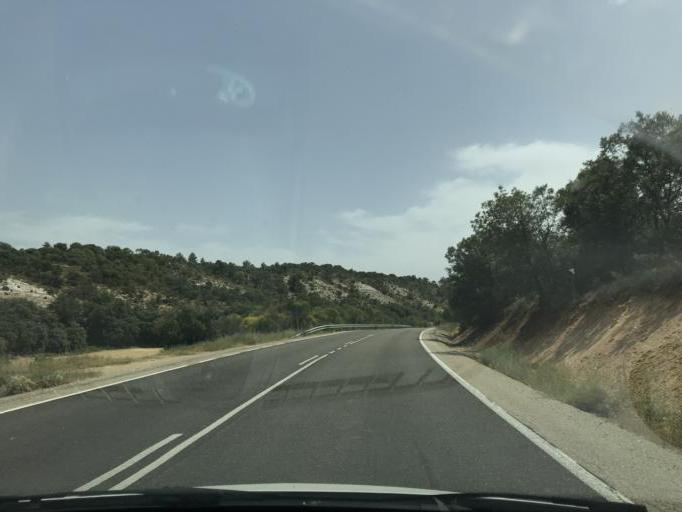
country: ES
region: Castille-La Mancha
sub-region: Provincia de Cuenca
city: La Frontera
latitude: 40.4020
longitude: -2.2467
